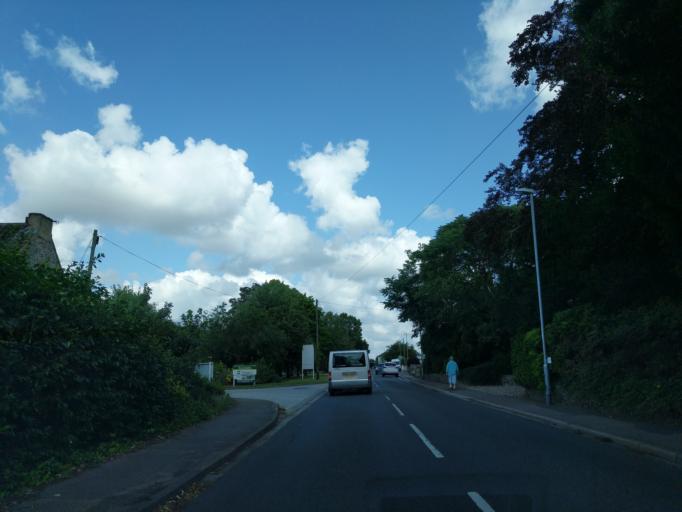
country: GB
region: England
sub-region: Suffolk
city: Exning
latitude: 52.3089
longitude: 0.3832
